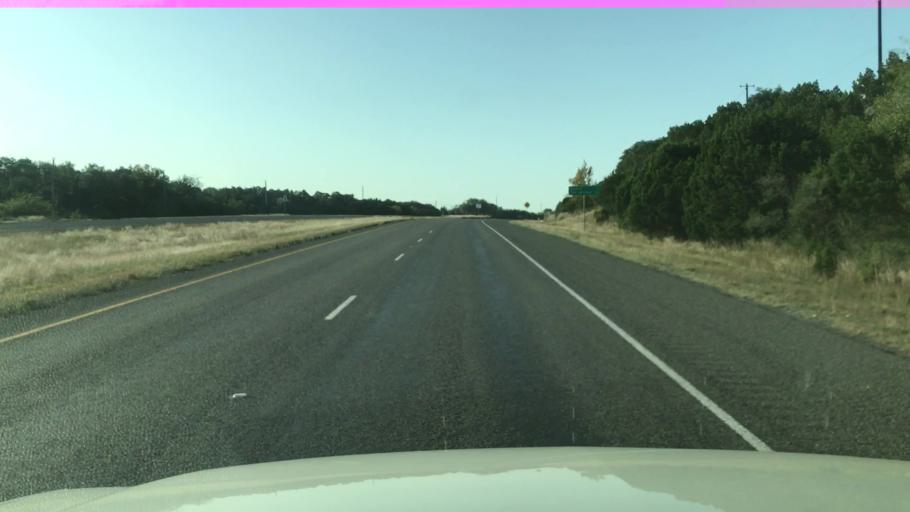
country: US
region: Texas
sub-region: Blanco County
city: Johnson City
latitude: 30.1981
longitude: -98.3759
